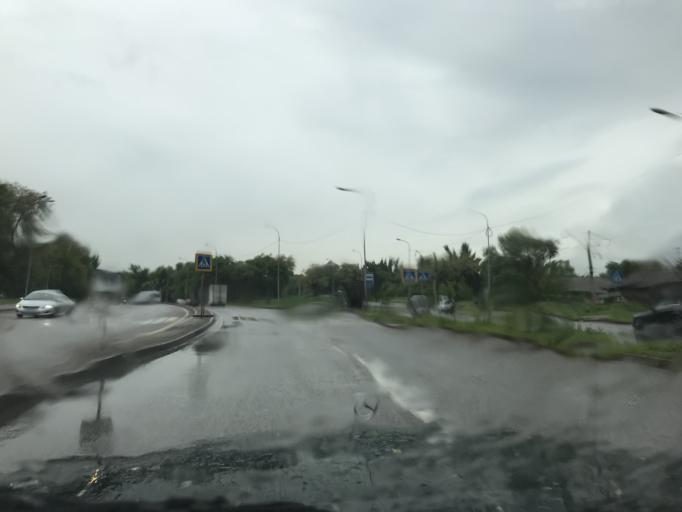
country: KZ
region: Almaty Oblysy
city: Pervomayskiy
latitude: 43.3333
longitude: 76.9606
